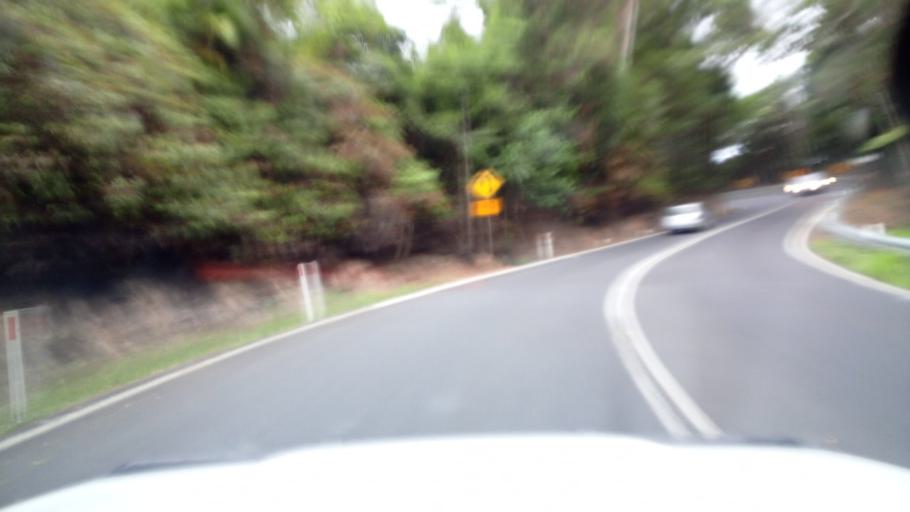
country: AU
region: Queensland
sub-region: Tablelands
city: Kuranda
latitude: -16.8318
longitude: 145.6633
